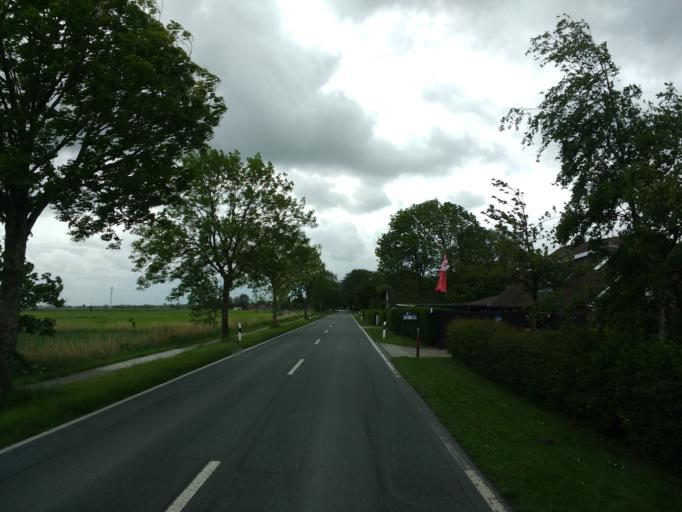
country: DE
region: Lower Saxony
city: Schillig
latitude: 53.6703
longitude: 7.9864
